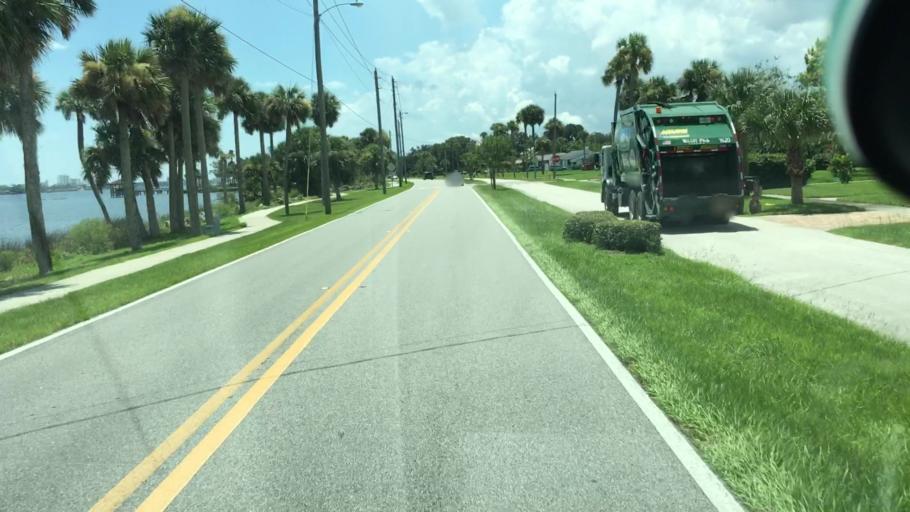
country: US
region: Florida
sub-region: Volusia County
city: Ormond Beach
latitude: 29.2669
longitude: -81.0463
